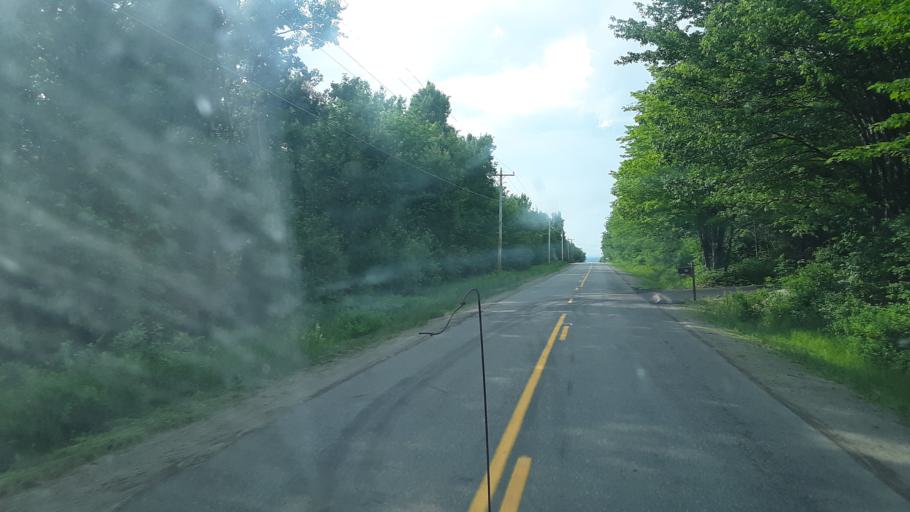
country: US
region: Maine
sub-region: Washington County
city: Calais
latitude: 45.0894
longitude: -67.5042
